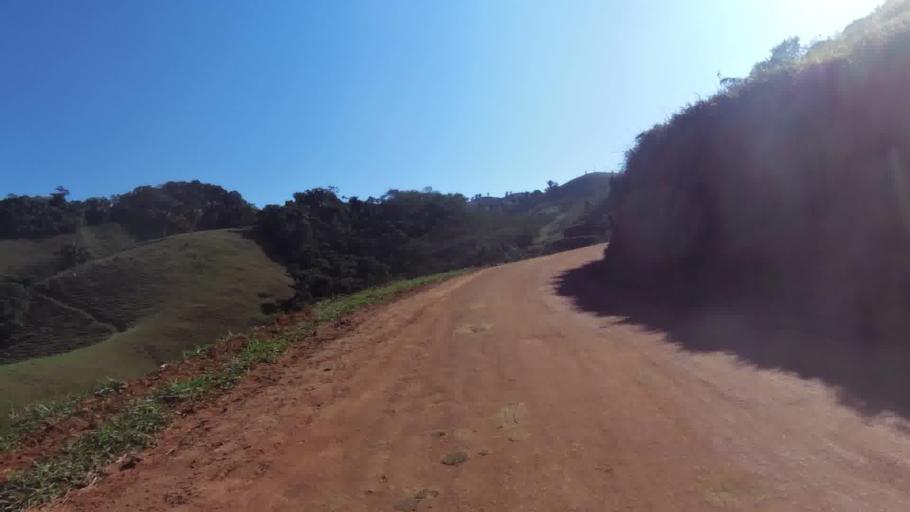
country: BR
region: Espirito Santo
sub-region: Alfredo Chaves
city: Alfredo Chaves
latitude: -20.6740
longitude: -40.7824
